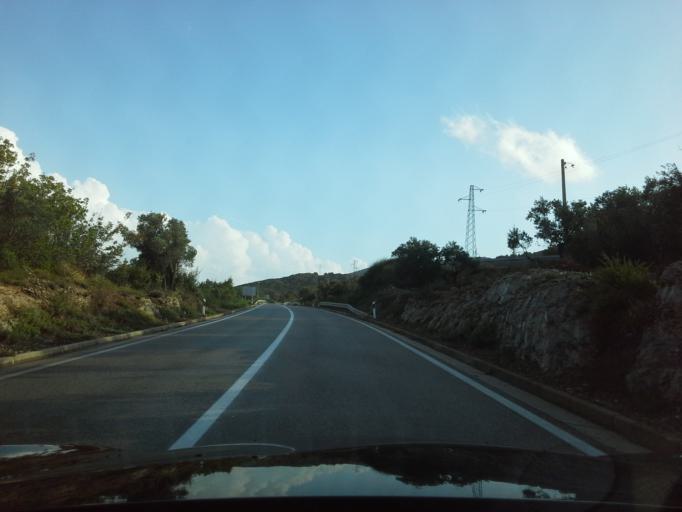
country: HR
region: Primorsko-Goranska
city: Mali Losinj
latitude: 44.6614
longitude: 14.3899
